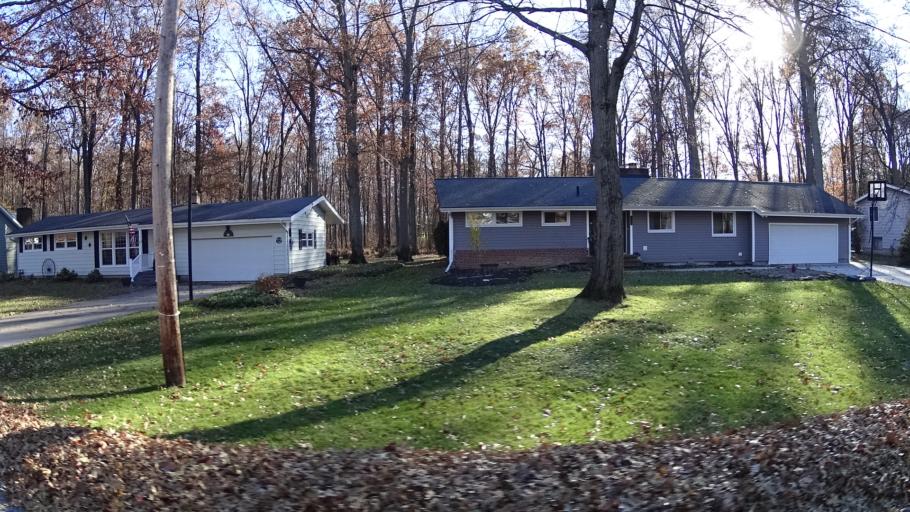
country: US
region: Ohio
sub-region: Lorain County
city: Avon Center
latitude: 41.4489
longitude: -81.9959
